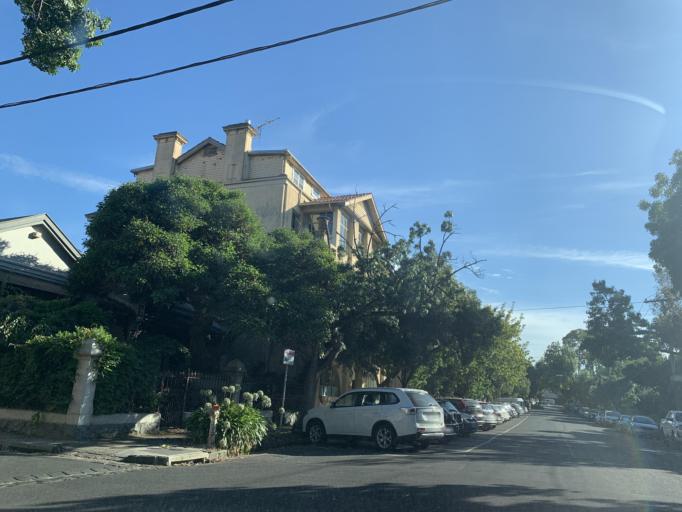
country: AU
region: Victoria
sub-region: Port Phillip
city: Saint Kilda
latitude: -37.8643
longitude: 144.9787
